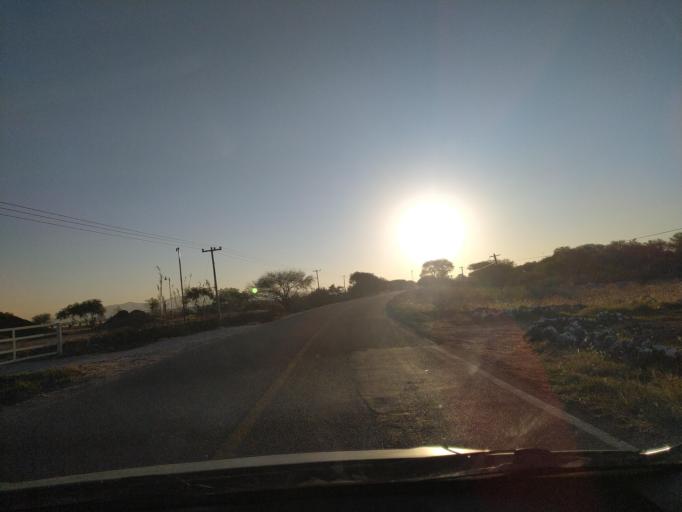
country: MX
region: Guanajuato
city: Ciudad Manuel Doblado
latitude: 20.7412
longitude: -101.9401
